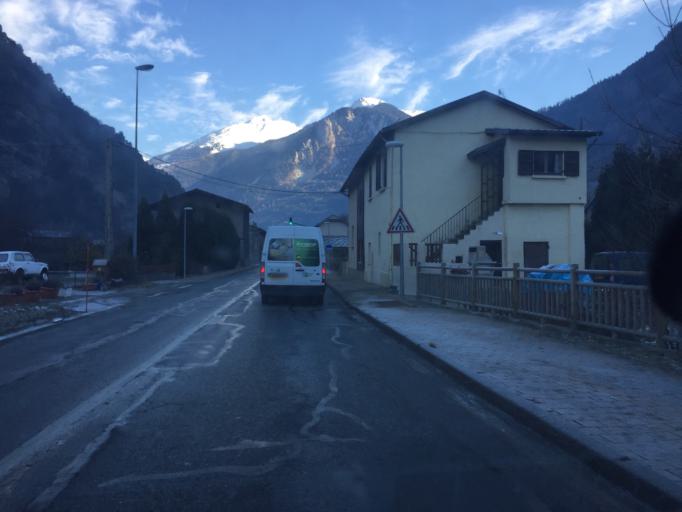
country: FR
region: Rhone-Alpes
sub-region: Departement de la Savoie
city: Modane
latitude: 45.1950
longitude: 6.6265
